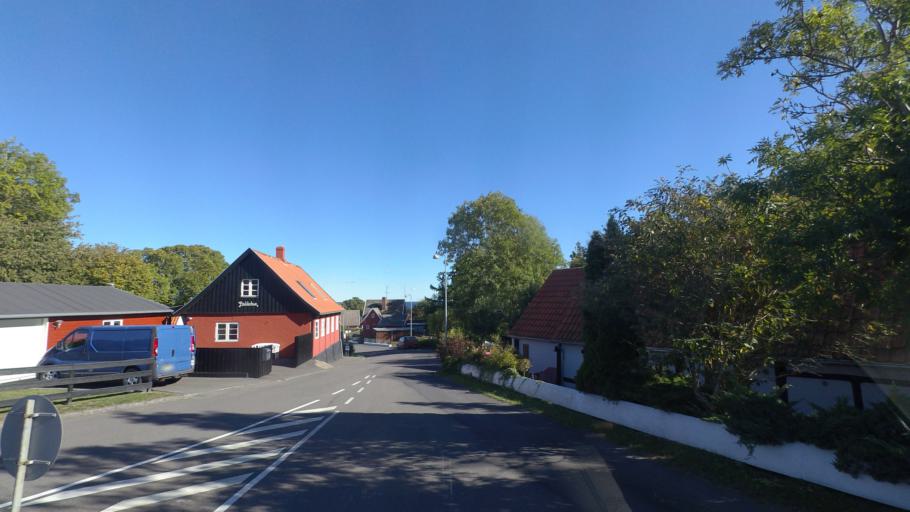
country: DK
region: Capital Region
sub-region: Bornholm Kommune
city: Nexo
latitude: 55.1097
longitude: 15.1404
